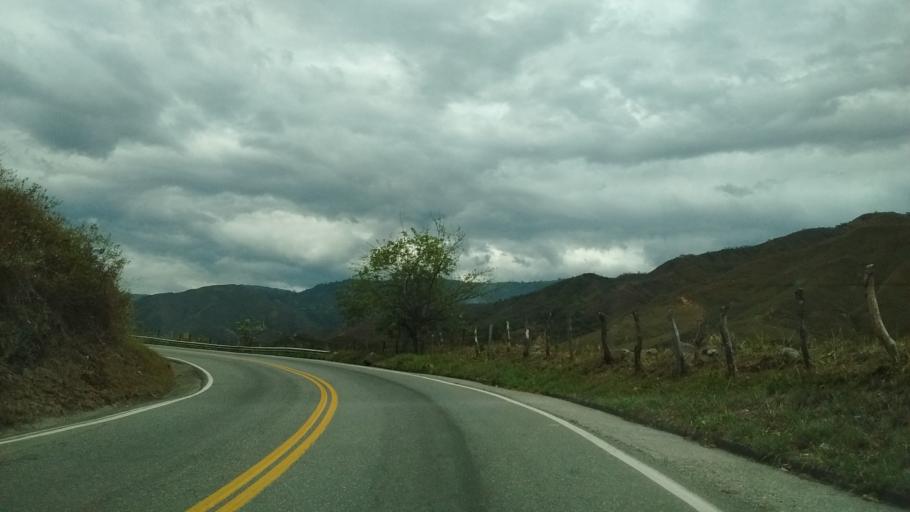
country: CO
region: Cauca
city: La Sierra
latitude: 2.2066
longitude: -76.8027
